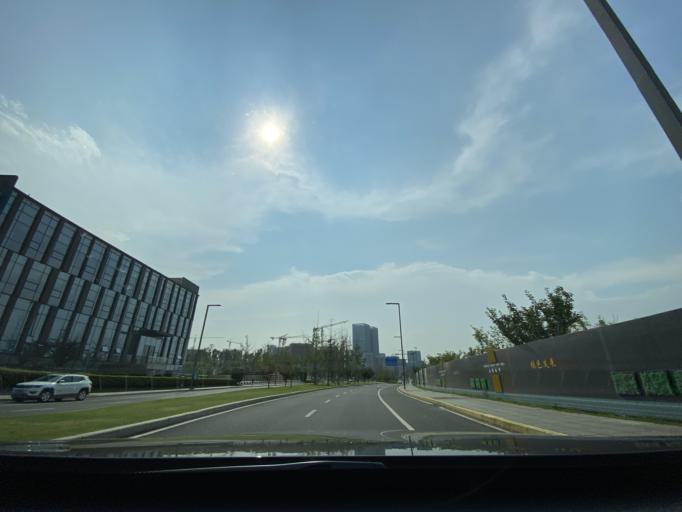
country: CN
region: Sichuan
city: Dongsheng
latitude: 30.3937
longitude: 104.0793
